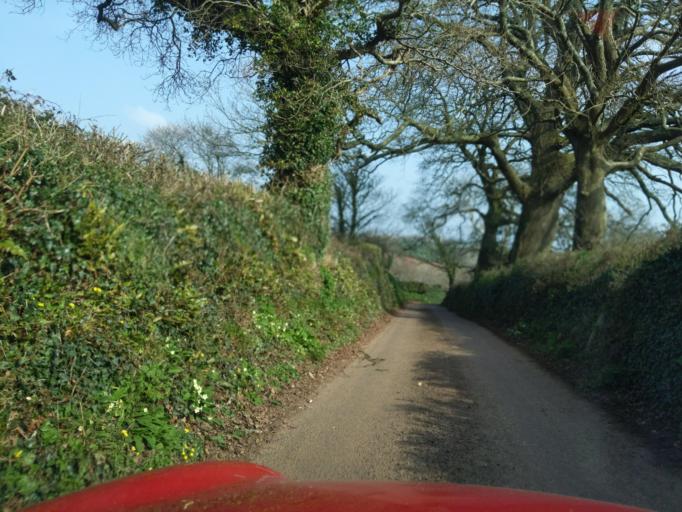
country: GB
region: England
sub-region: Devon
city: Kingsbridge
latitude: 50.2868
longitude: -3.7276
